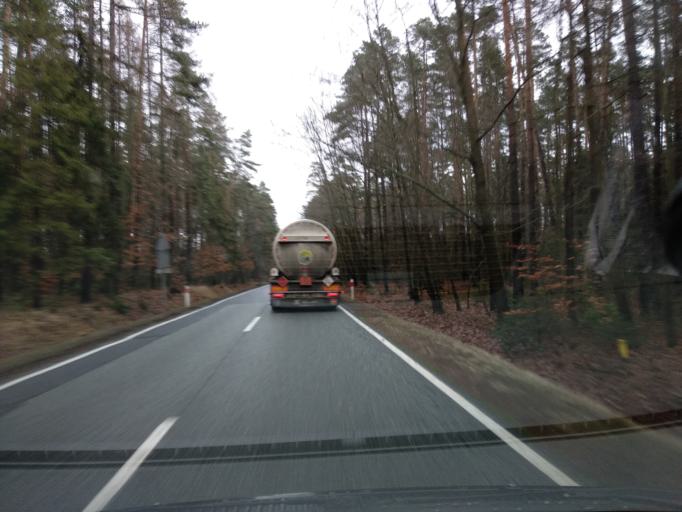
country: PL
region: Lower Silesian Voivodeship
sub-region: Powiat olesnicki
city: Twardogora
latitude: 51.3223
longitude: 17.5684
